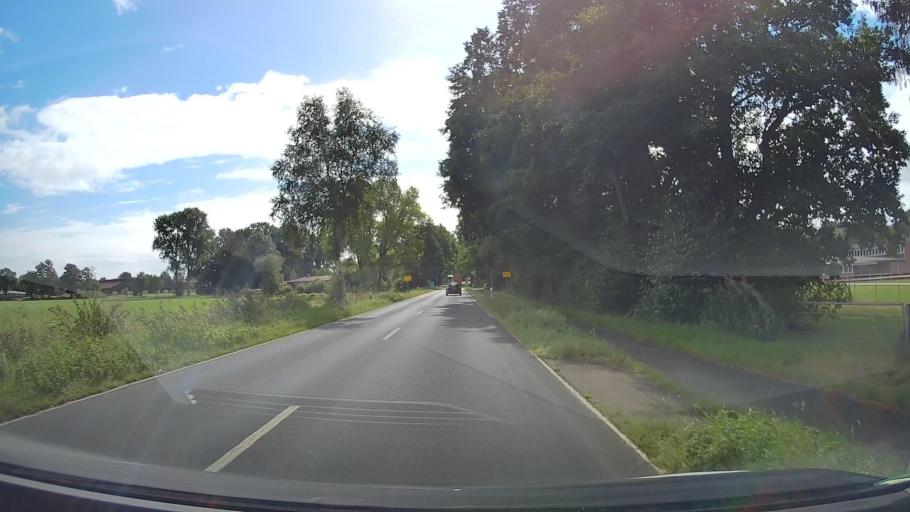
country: DE
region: Lower Saxony
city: Rhade
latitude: 53.3314
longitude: 9.1129
